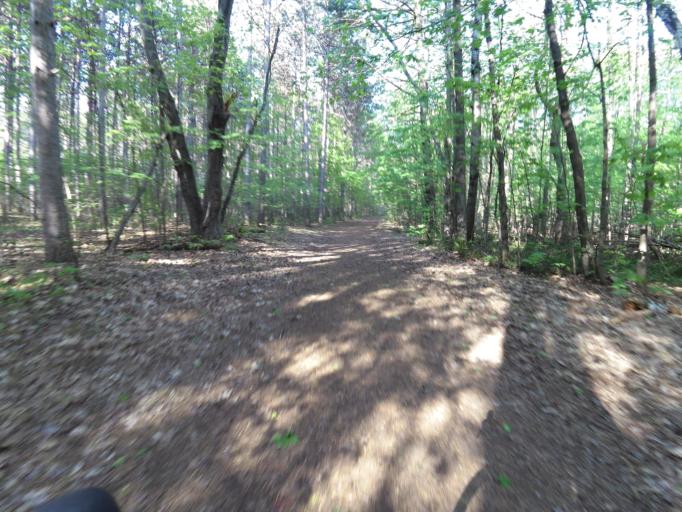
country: CA
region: Ontario
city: Bells Corners
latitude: 45.3261
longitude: -75.7399
